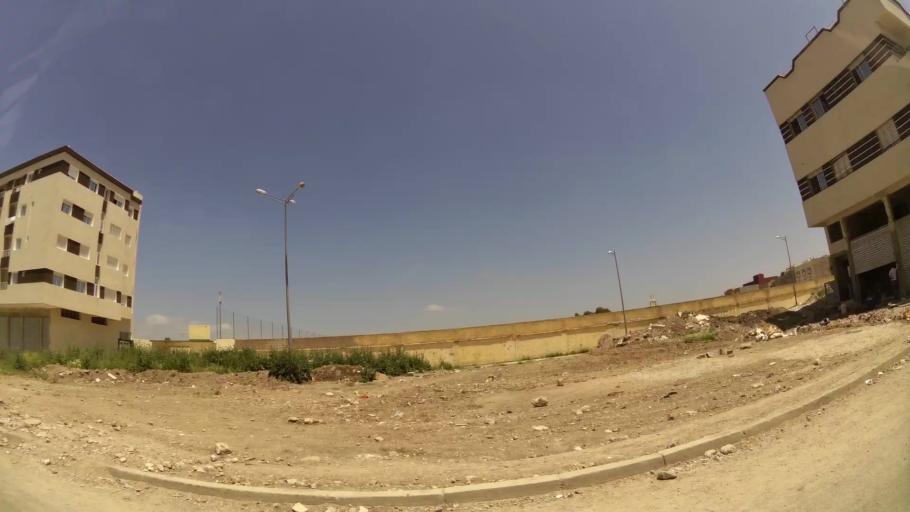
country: MA
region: Fes-Boulemane
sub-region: Fes
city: Fes
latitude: 34.0361
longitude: -5.0440
